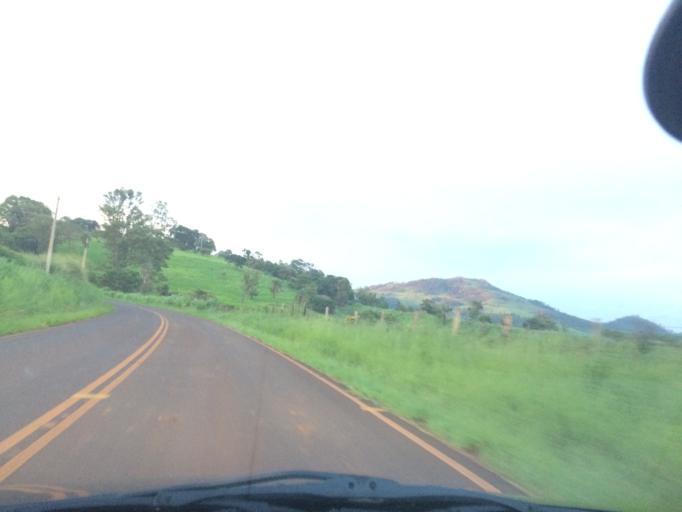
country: BR
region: Sao Paulo
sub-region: Tambau
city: Tambau
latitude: -21.7104
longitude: -47.1968
